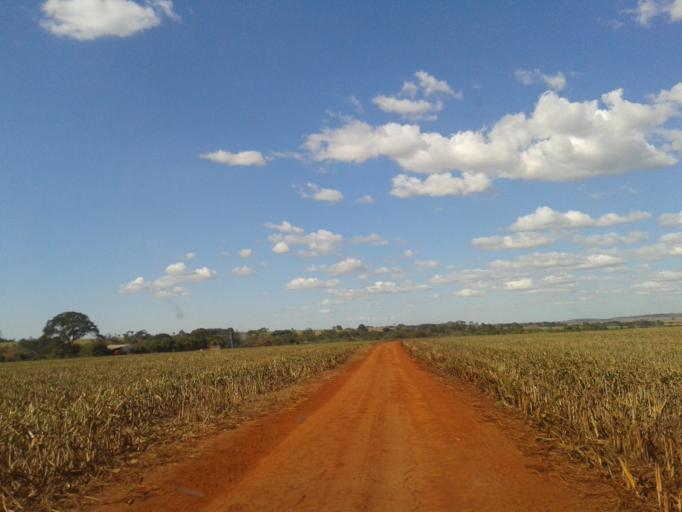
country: BR
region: Minas Gerais
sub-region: Centralina
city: Centralina
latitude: -18.5958
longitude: -49.2660
